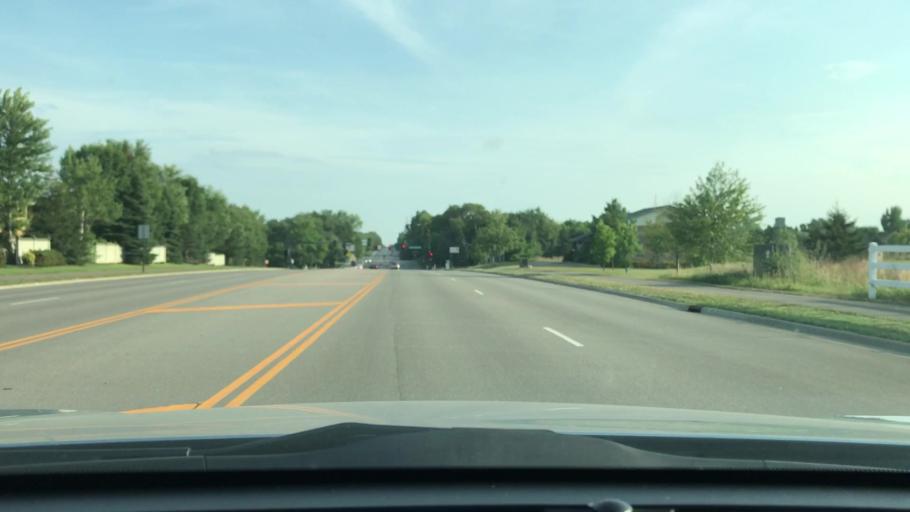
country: US
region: Minnesota
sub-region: Hennepin County
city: Maple Grove
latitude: 45.0456
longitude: -93.4818
